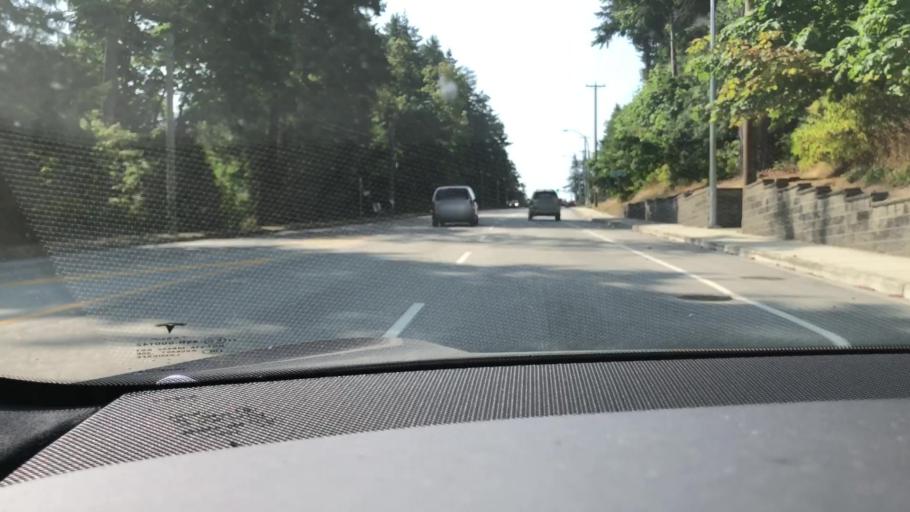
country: US
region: Washington
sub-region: Whatcom County
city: Point Roberts
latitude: 49.0065
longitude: -123.0687
